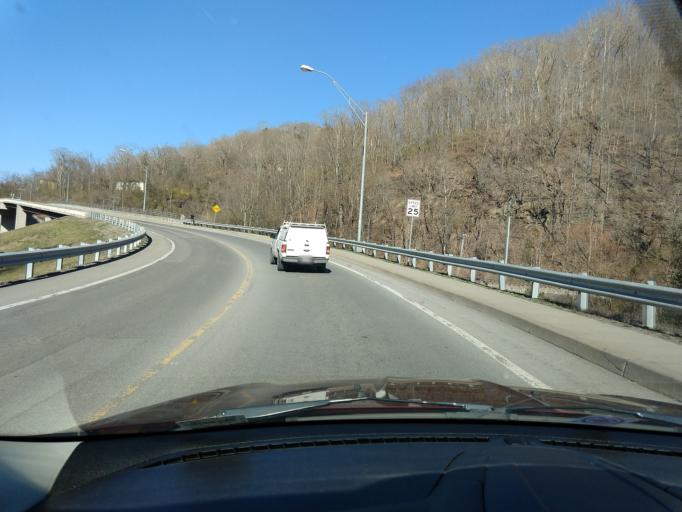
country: US
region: West Virginia
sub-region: Summers County
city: Hinton
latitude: 37.6682
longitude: -80.8915
